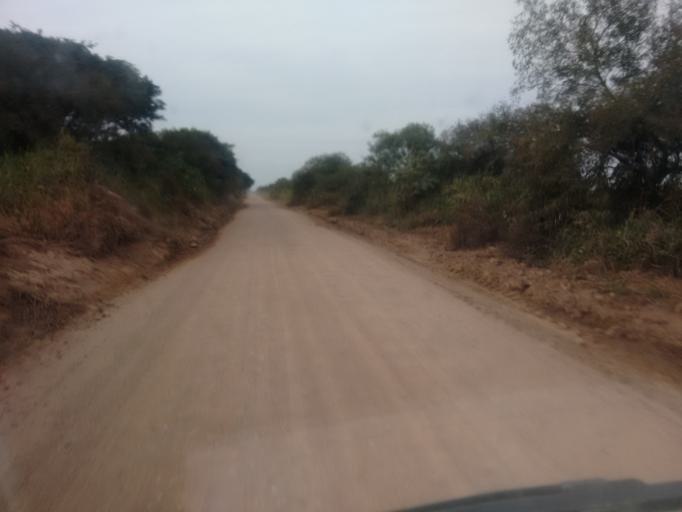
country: BR
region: Rio Grande do Sul
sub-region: Camaqua
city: Camaqua
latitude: -30.9510
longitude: -51.7875
